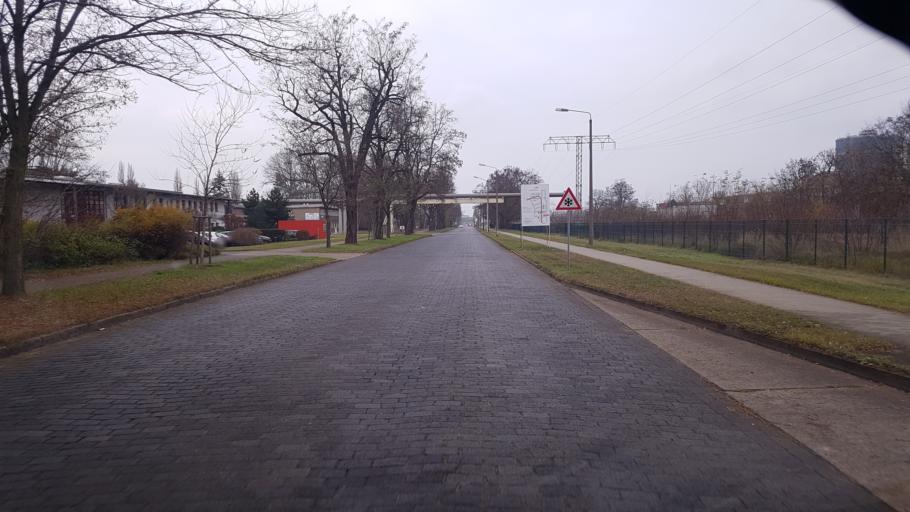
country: DE
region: Brandenburg
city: Eisenhuettenstadt
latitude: 52.1604
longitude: 14.6329
